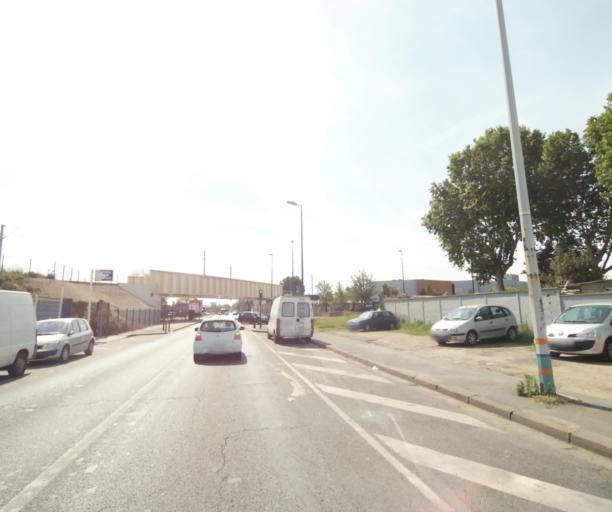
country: FR
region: Ile-de-France
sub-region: Departement des Hauts-de-Seine
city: Gennevilliers
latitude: 48.9300
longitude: 2.3087
